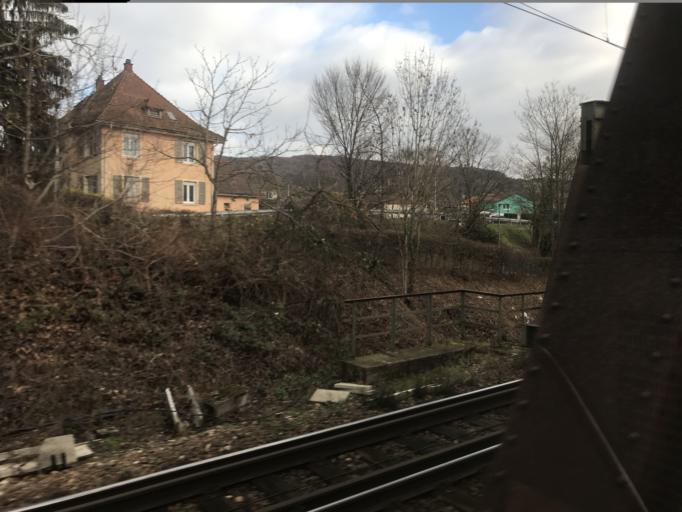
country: DE
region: Baden-Wuerttemberg
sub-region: Freiburg Region
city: Weil am Rhein
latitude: 47.6113
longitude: 7.6136
